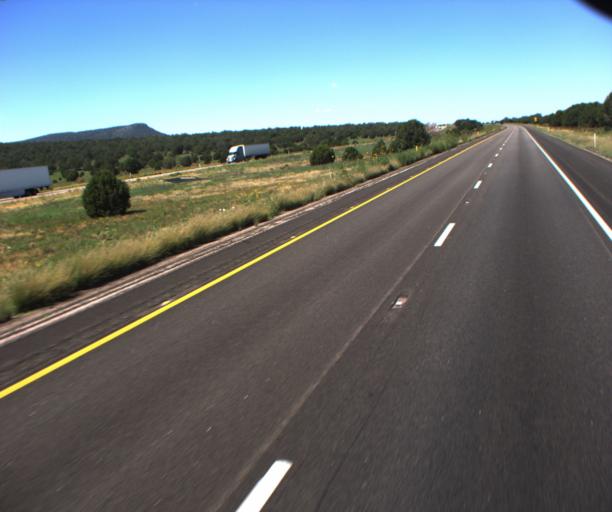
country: US
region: Arizona
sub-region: Mohave County
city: Peach Springs
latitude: 35.2281
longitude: -113.2307
